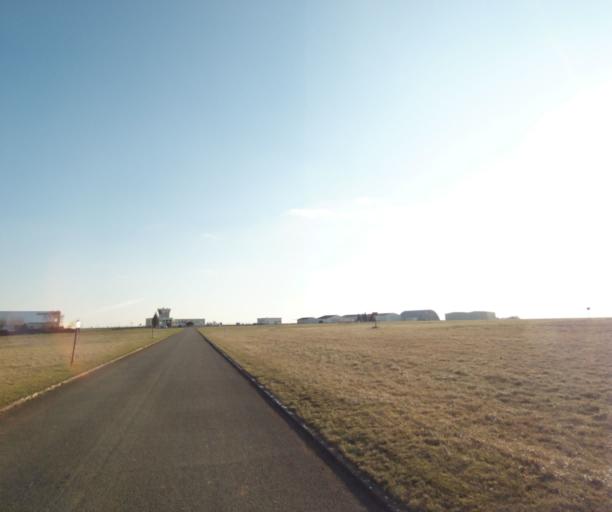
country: FR
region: Poitou-Charentes
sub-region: Departement des Deux-Sevres
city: Vouille
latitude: 46.3174
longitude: -0.3994
